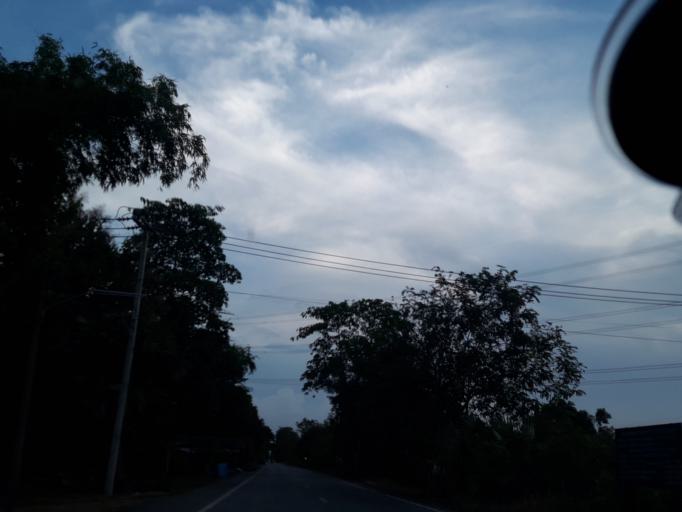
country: TH
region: Pathum Thani
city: Nong Suea
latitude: 14.1853
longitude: 100.8689
